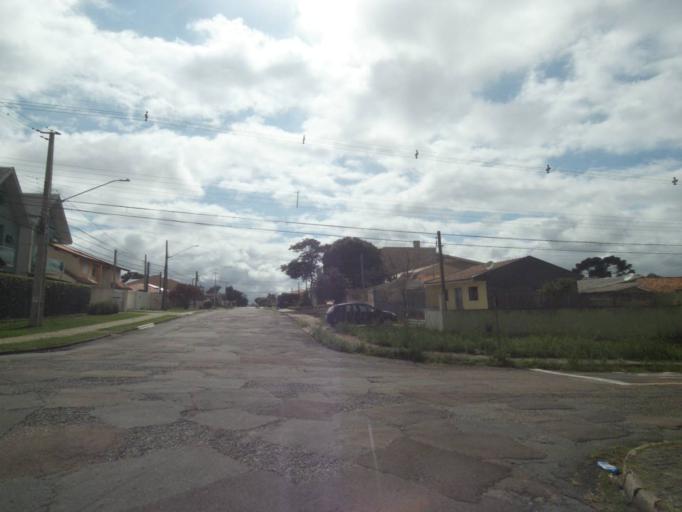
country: BR
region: Parana
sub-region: Pinhais
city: Pinhais
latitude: -25.4537
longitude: -49.2233
